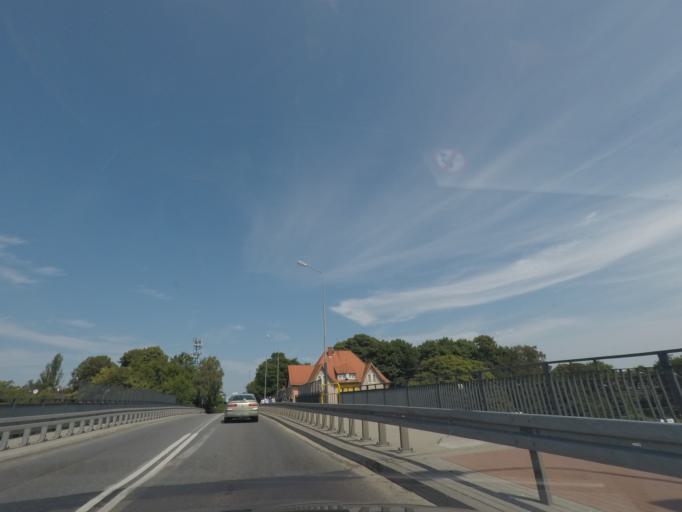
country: PL
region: Pomeranian Voivodeship
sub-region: Powiat slupski
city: Ustka
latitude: 54.5789
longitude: 16.8599
